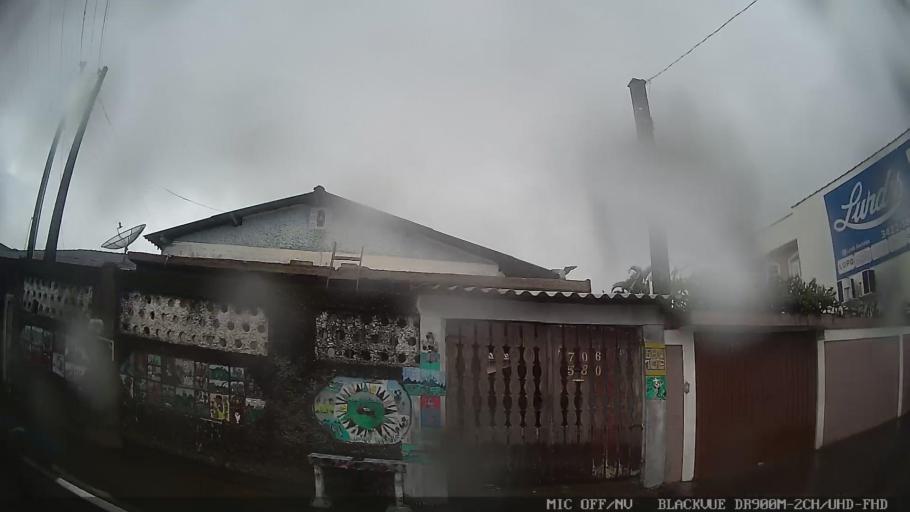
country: BR
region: Sao Paulo
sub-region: Itanhaem
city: Itanhaem
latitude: -24.1753
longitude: -46.7873
